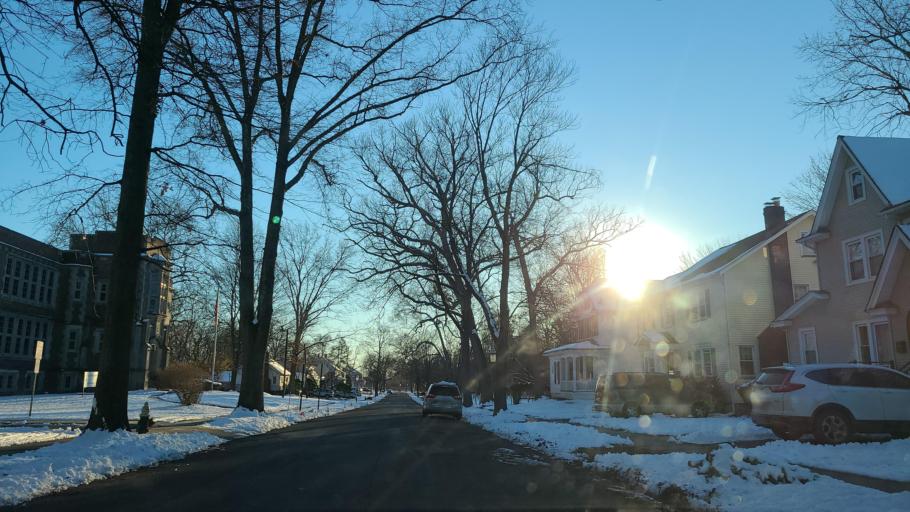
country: US
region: New Jersey
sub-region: Essex County
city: South Orange
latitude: 40.7547
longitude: -74.2560
